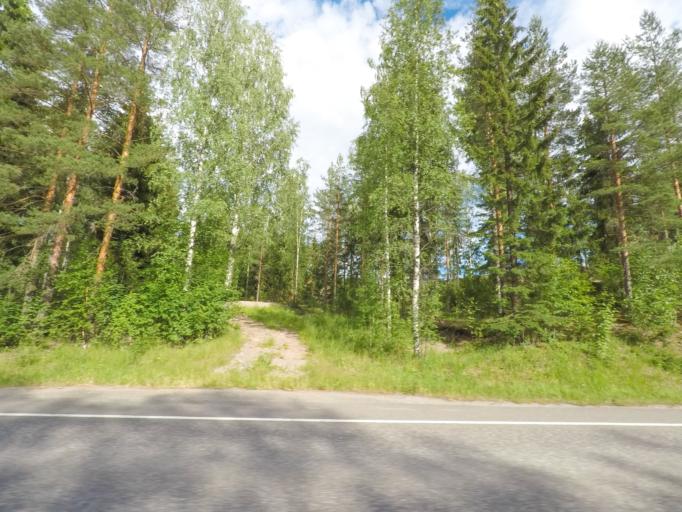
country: FI
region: Uusimaa
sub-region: Porvoo
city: Pukkila
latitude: 60.8081
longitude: 25.4805
